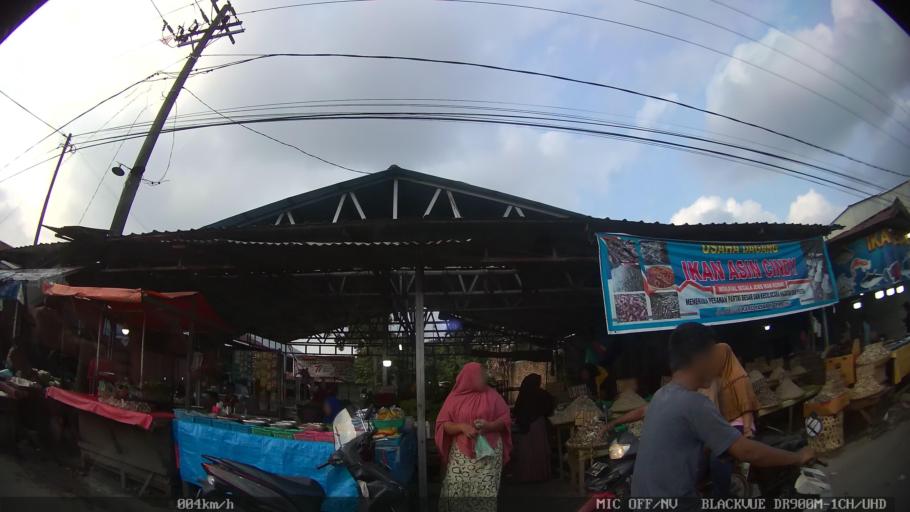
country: ID
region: North Sumatra
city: Medan
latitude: 3.5814
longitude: 98.7406
